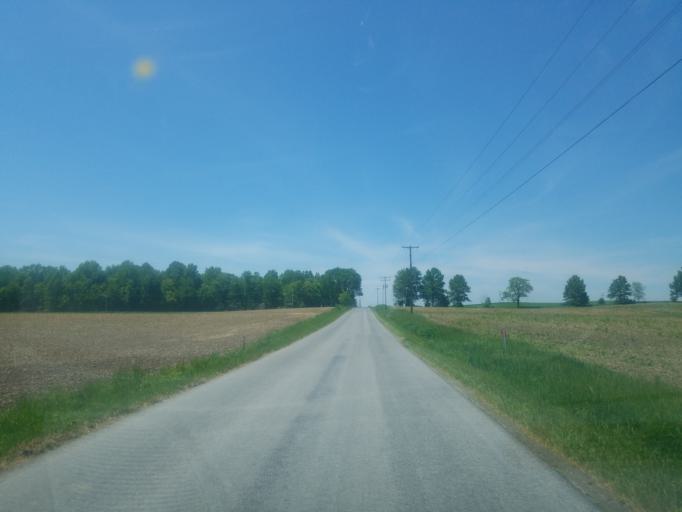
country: US
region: Ohio
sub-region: Huron County
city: Greenwich
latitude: 40.9929
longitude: -82.4757
